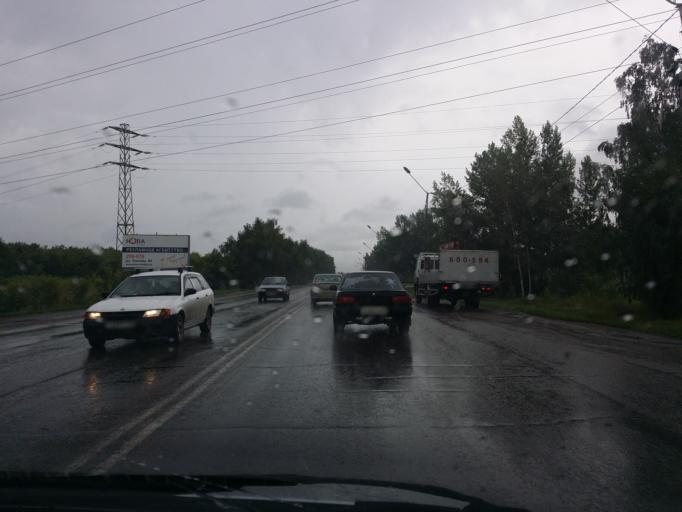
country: RU
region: Altai Krai
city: Novosilikatnyy
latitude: 53.3491
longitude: 83.6220
